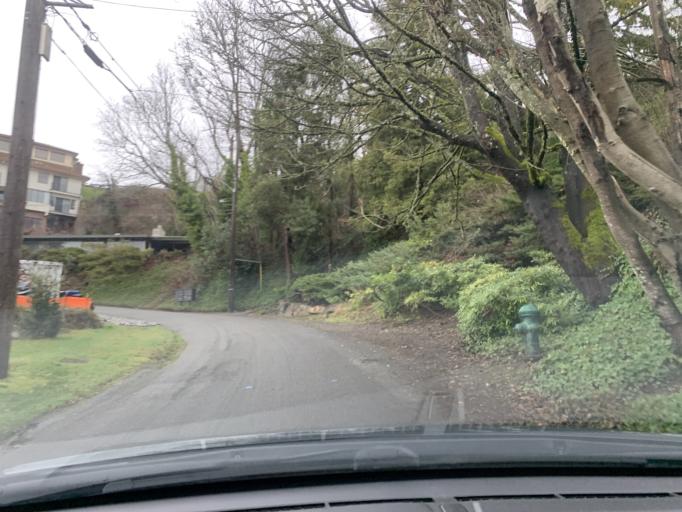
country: US
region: Washington
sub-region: King County
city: White Center
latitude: 47.5618
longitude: -122.3995
